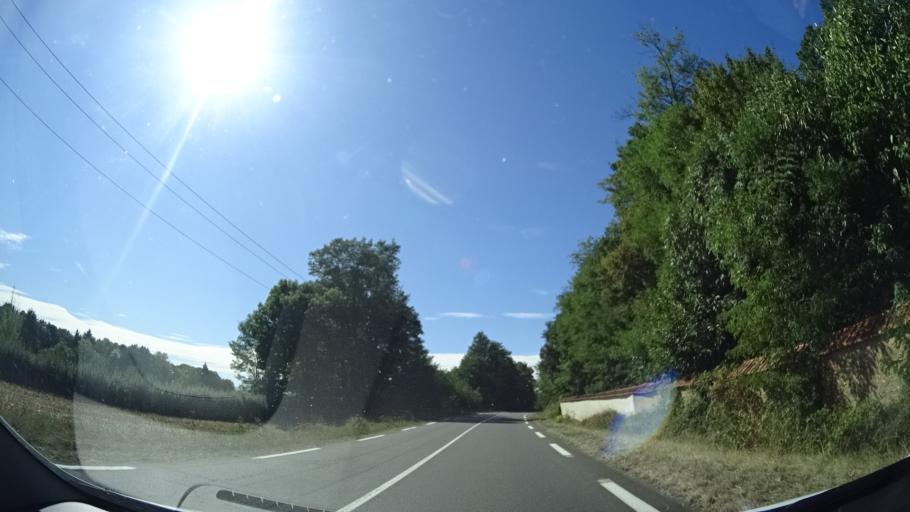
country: FR
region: Centre
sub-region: Departement du Loiret
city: Douchy
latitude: 47.9455
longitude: 3.0358
